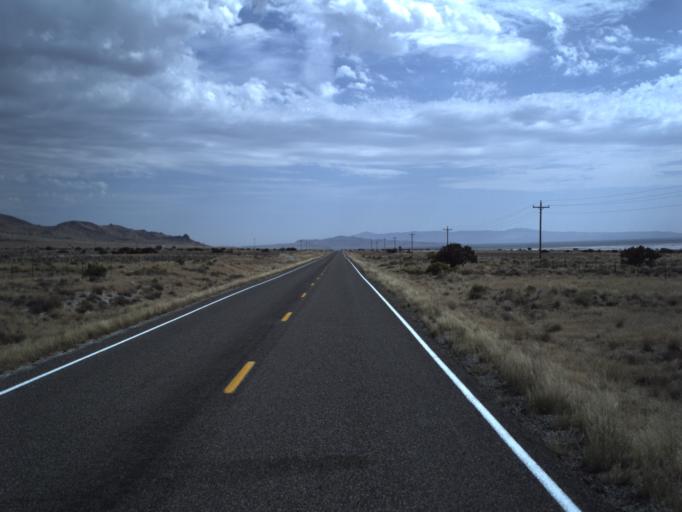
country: US
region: Utah
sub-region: Tooele County
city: Wendover
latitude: 41.4359
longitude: -113.7521
